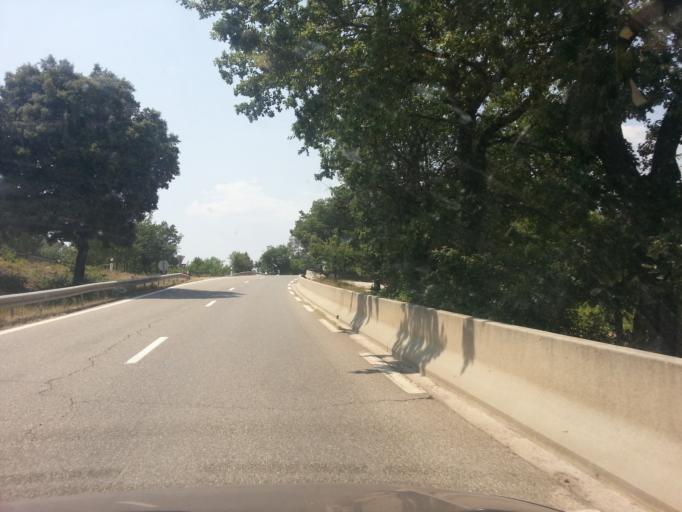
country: FR
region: Provence-Alpes-Cote d'Azur
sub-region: Departement du Var
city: Camps-la-Source
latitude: 43.4008
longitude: 6.1107
